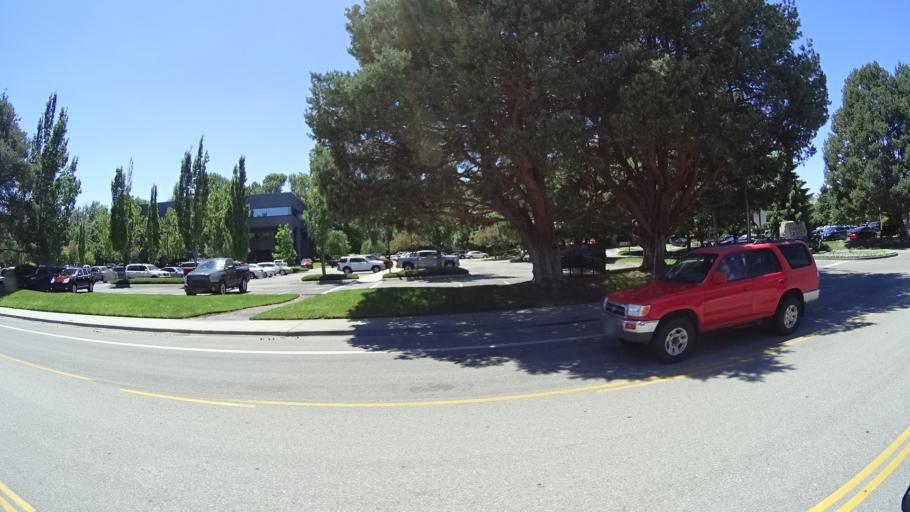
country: US
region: Idaho
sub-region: Ada County
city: Boise
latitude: 43.6122
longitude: -116.2116
